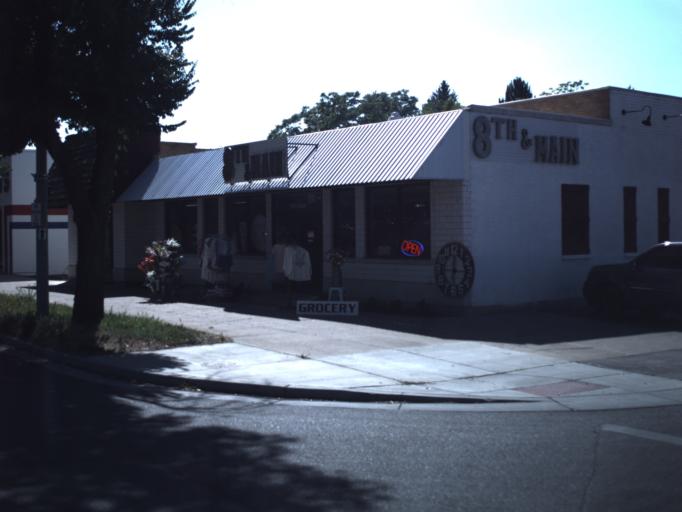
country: US
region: Utah
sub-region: Cache County
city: Logan
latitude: 41.7464
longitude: -111.8347
